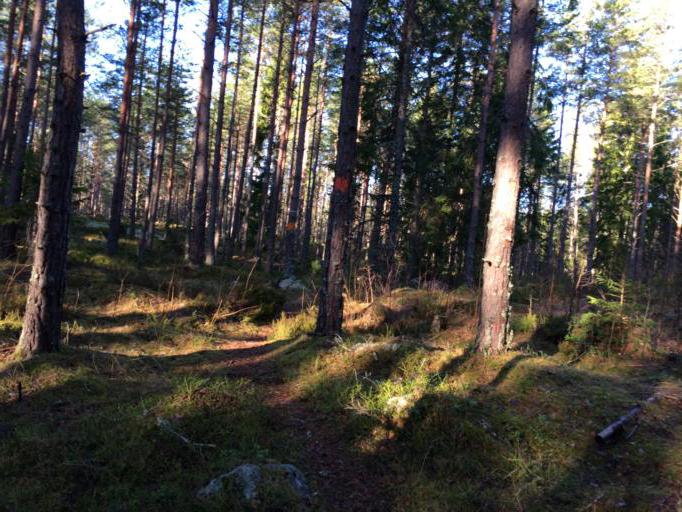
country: SE
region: Vaestmanland
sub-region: Hallstahammars Kommun
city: Hallstahammar
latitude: 59.6351
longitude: 16.2643
